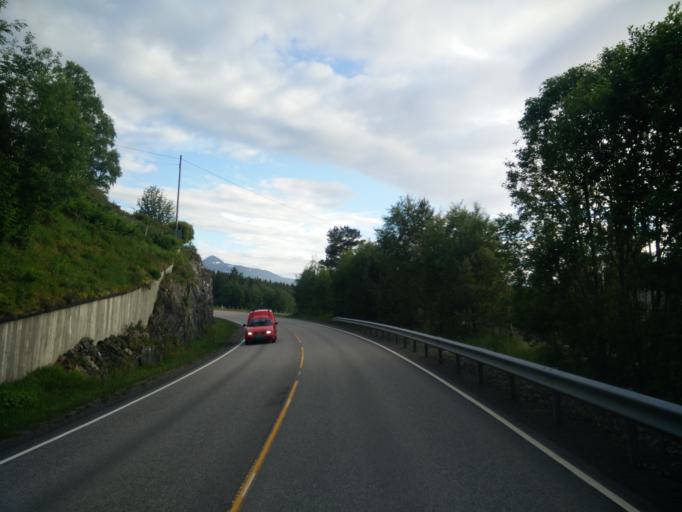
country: NO
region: More og Romsdal
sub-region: Kristiansund
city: Rensvik
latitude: 63.0166
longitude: 8.0044
